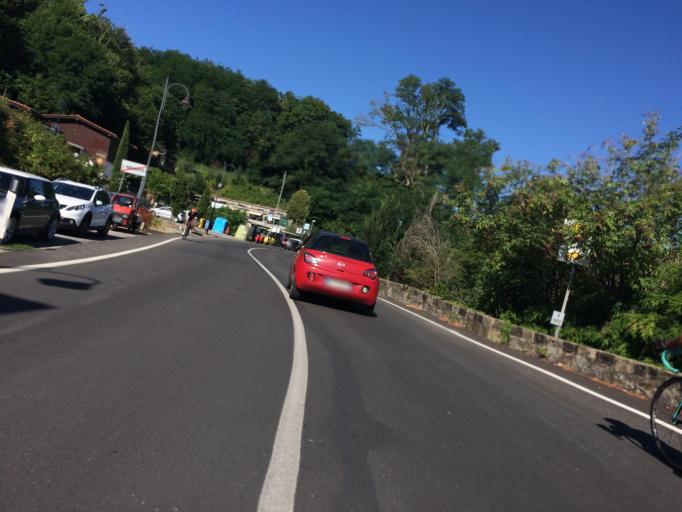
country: IT
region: Liguria
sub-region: Provincia di Genova
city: Camogli
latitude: 44.3439
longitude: 9.1808
